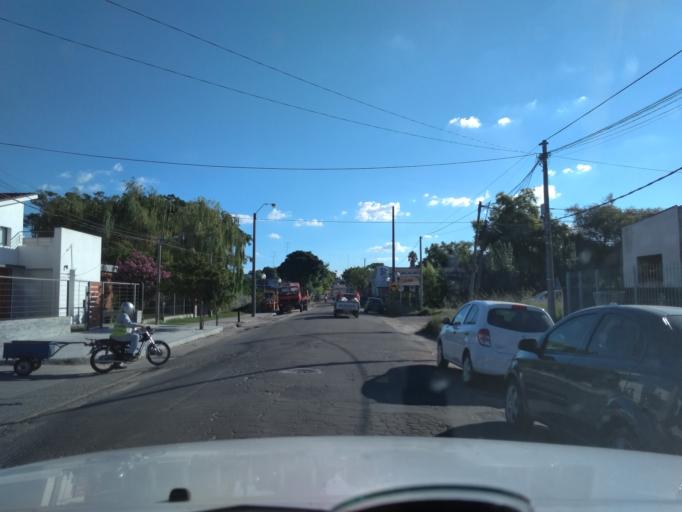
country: UY
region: Florida
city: Florida
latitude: -34.0965
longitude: -56.2241
